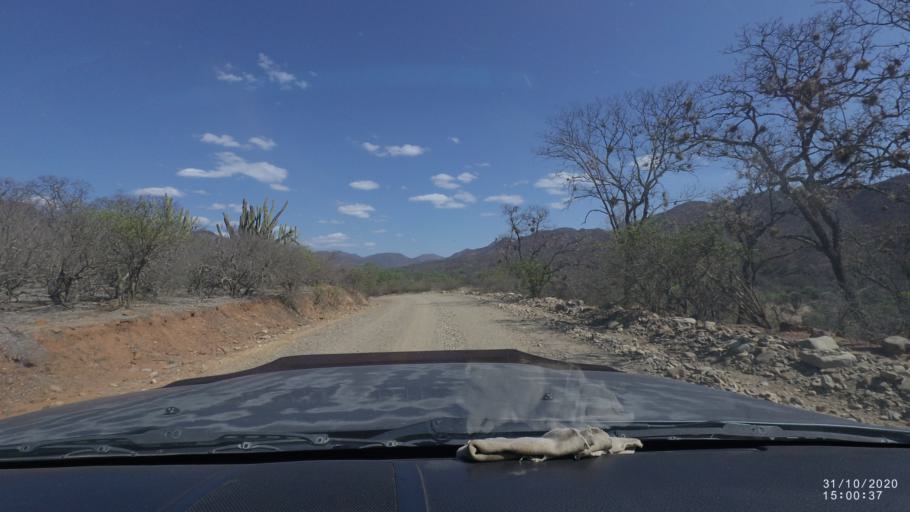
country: BO
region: Cochabamba
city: Aiquile
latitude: -18.2591
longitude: -64.8236
